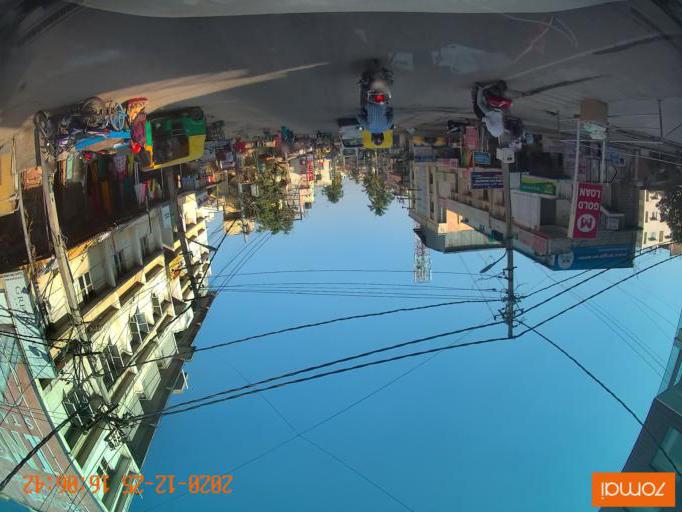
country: IN
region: Karnataka
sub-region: Bangalore Urban
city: Bangalore
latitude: 12.8927
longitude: 77.6259
